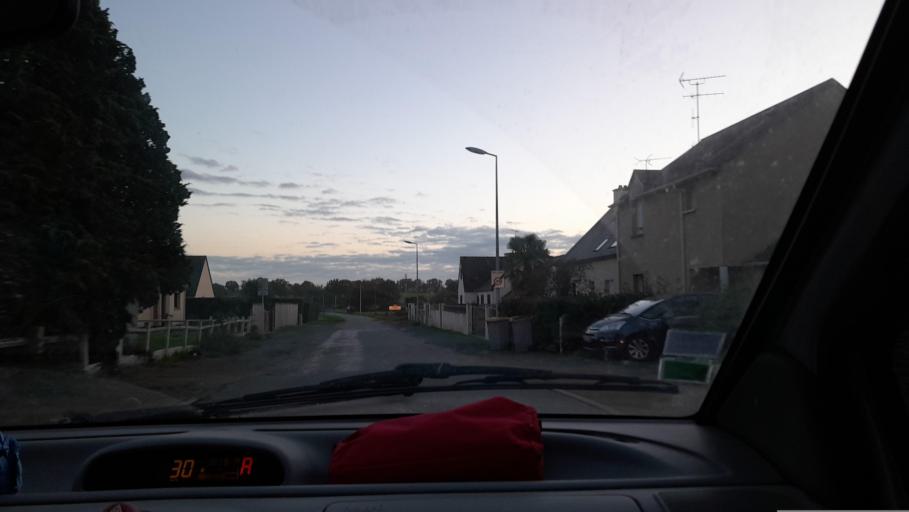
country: FR
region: Brittany
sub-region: Departement d'Ille-et-Vilaine
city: Rannee
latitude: 47.8846
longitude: -1.1802
